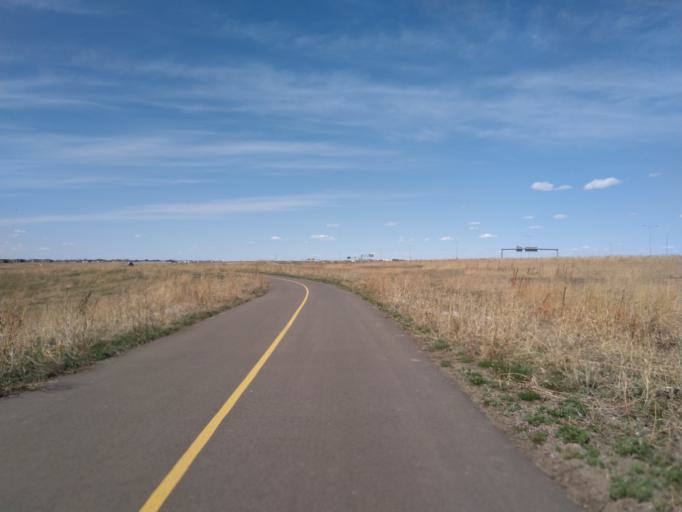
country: CA
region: Alberta
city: Chestermere
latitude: 51.0201
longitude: -113.9242
